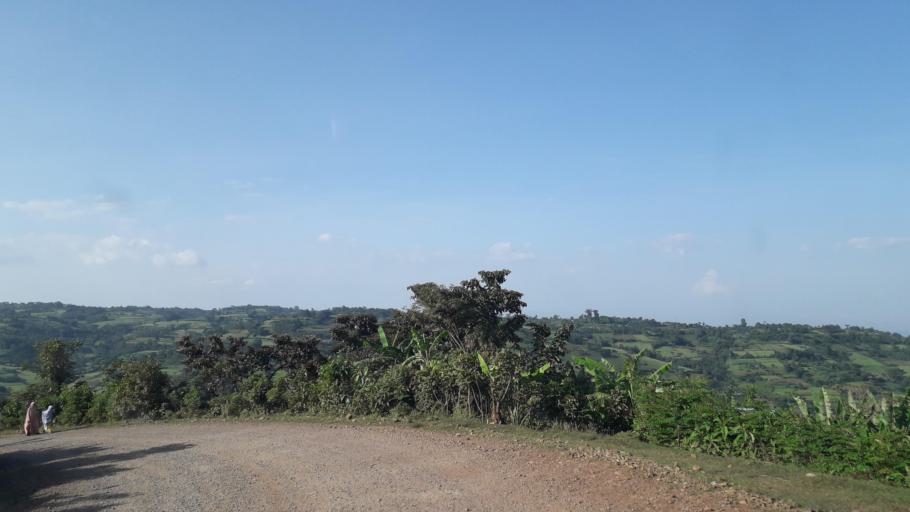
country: ET
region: Oromiya
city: Jima
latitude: 7.4713
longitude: 36.8786
